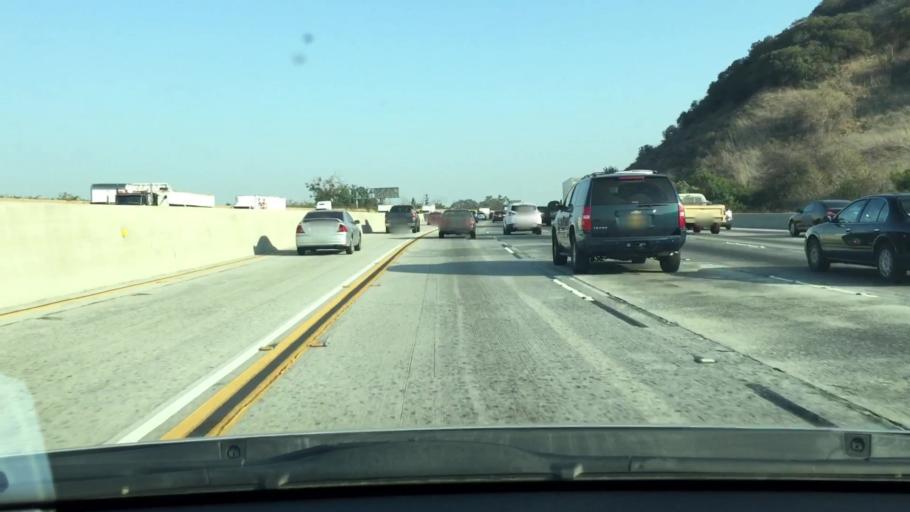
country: US
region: California
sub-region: Los Angeles County
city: Avocado Heights
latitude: 34.0286
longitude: -117.9973
